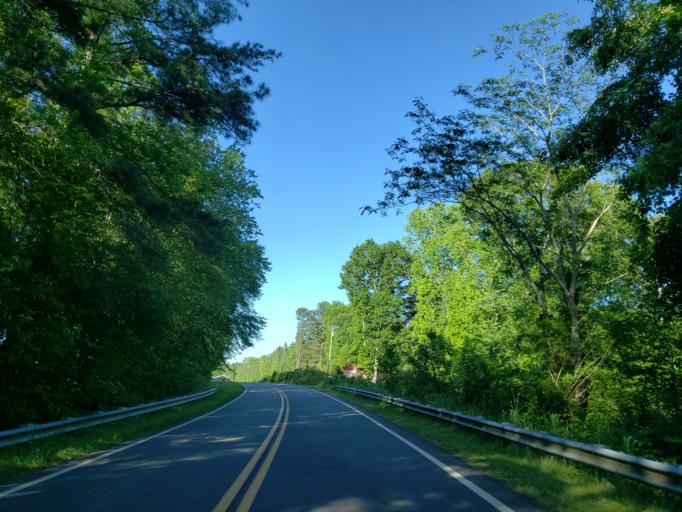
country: US
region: Georgia
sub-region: Haralson County
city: Buchanan
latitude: 33.7963
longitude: -85.2466
